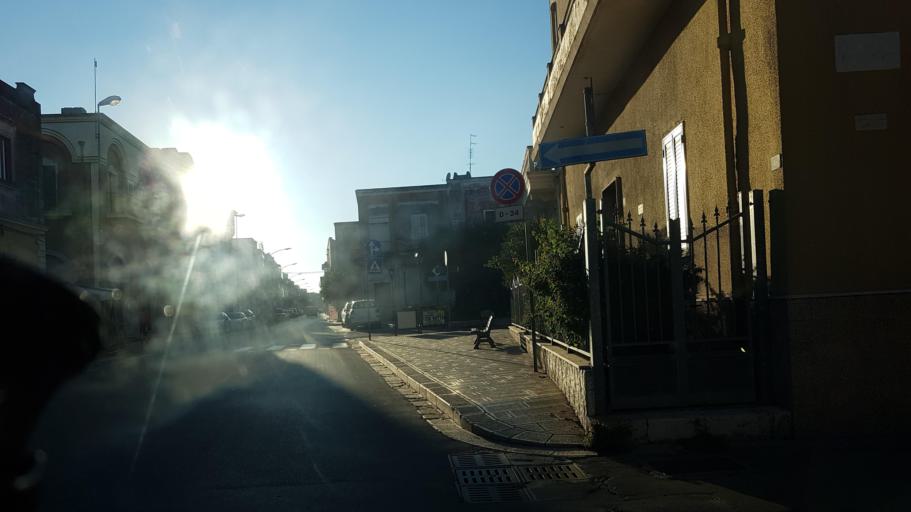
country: IT
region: Apulia
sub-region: Provincia di Brindisi
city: Latiano
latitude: 40.5517
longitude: 17.7176
